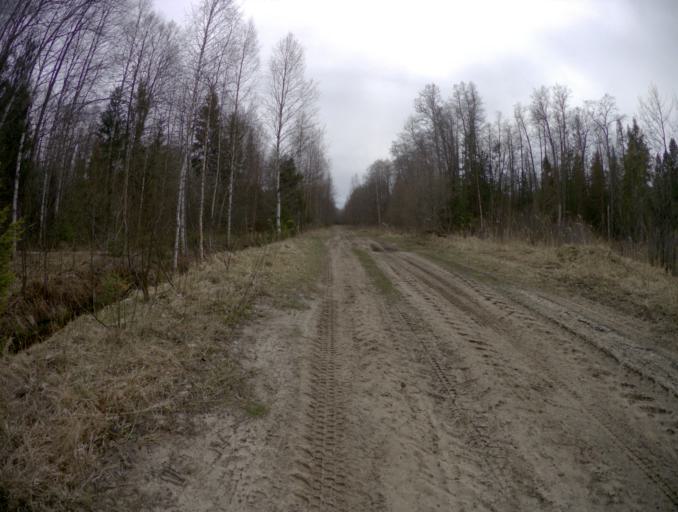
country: RU
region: Vladimir
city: Raduzhnyy
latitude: 55.9365
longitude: 40.2426
